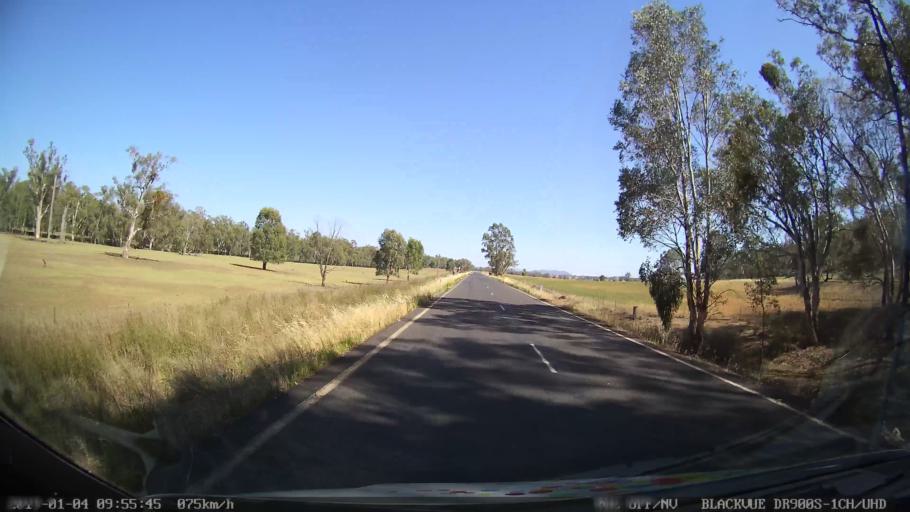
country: AU
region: New South Wales
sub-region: Cabonne
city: Canowindra
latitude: -33.5317
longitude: 148.4021
